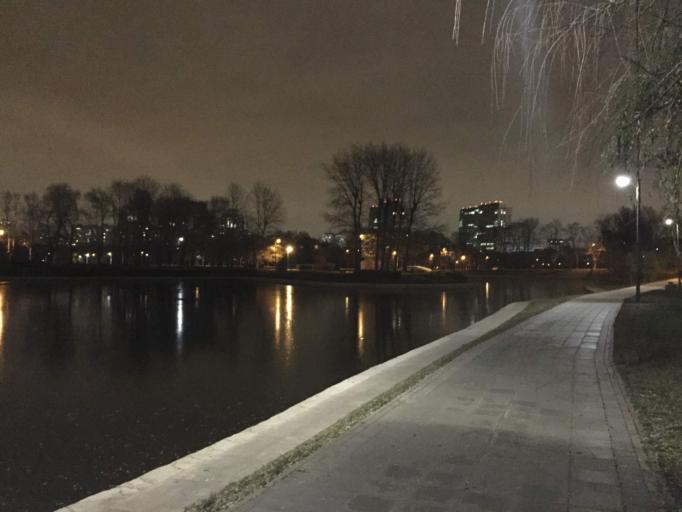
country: RU
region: Moskovskaya
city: Levoberezhnyy
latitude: 55.8517
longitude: 37.4833
